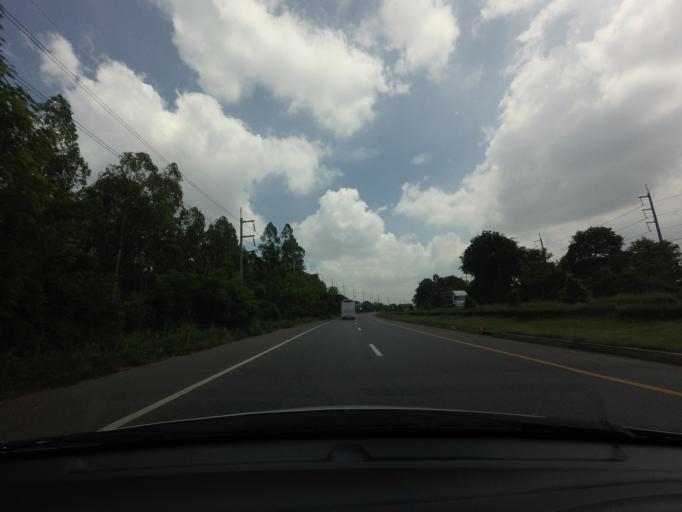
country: TH
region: Chachoengsao
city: Sanam Chai Khet
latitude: 13.7469
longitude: 101.4744
